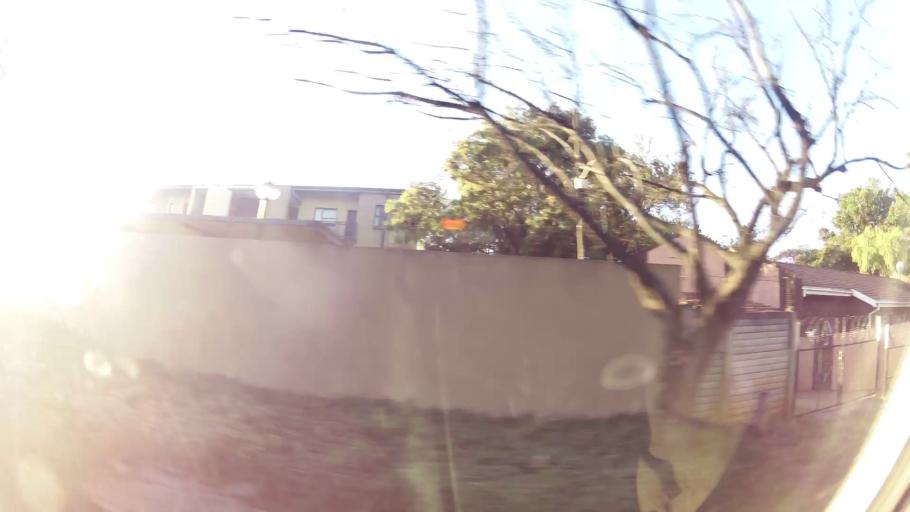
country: ZA
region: North-West
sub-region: Bojanala Platinum District Municipality
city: Rustenburg
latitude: -25.6744
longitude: 27.2103
